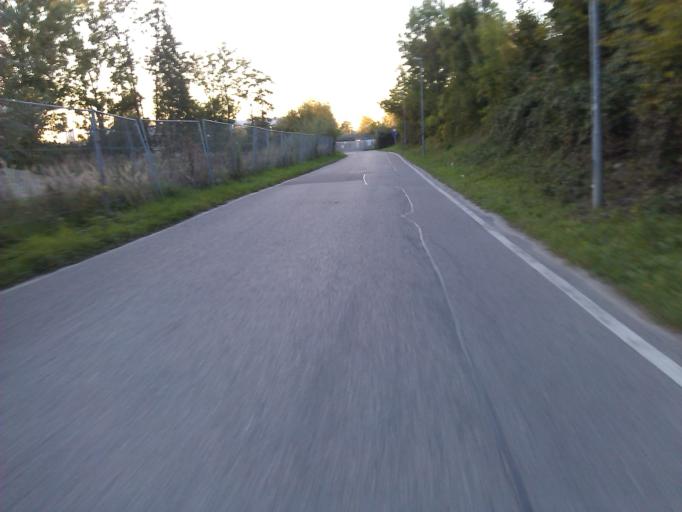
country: DE
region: Baden-Wuerttemberg
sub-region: Karlsruhe Region
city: Sinsheim
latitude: 49.2453
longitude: 8.8913
